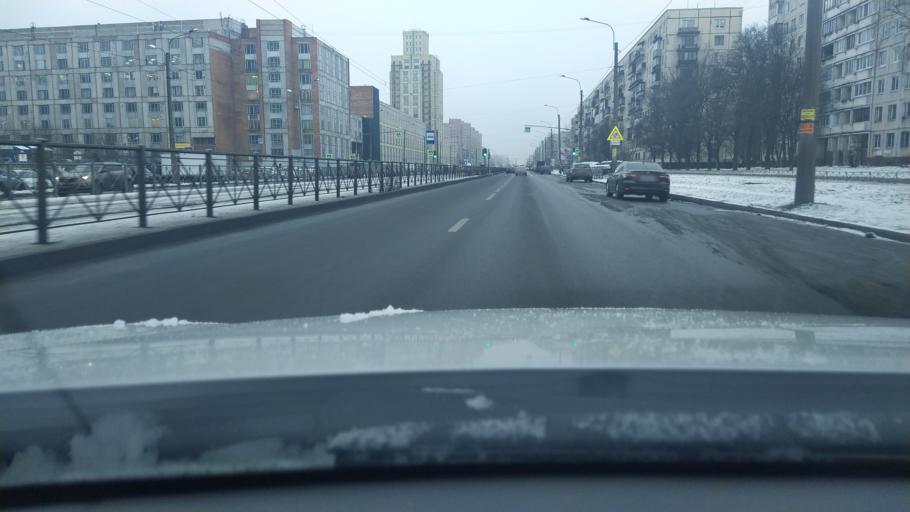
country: RU
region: St.-Petersburg
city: Grazhdanka
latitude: 60.0338
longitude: 30.4287
